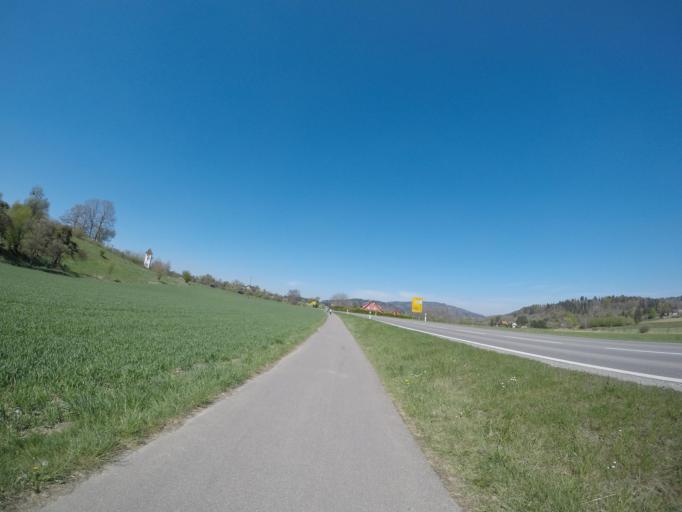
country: DE
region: Baden-Wuerttemberg
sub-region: Tuebingen Region
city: Markdorf
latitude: 47.7730
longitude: 9.4076
